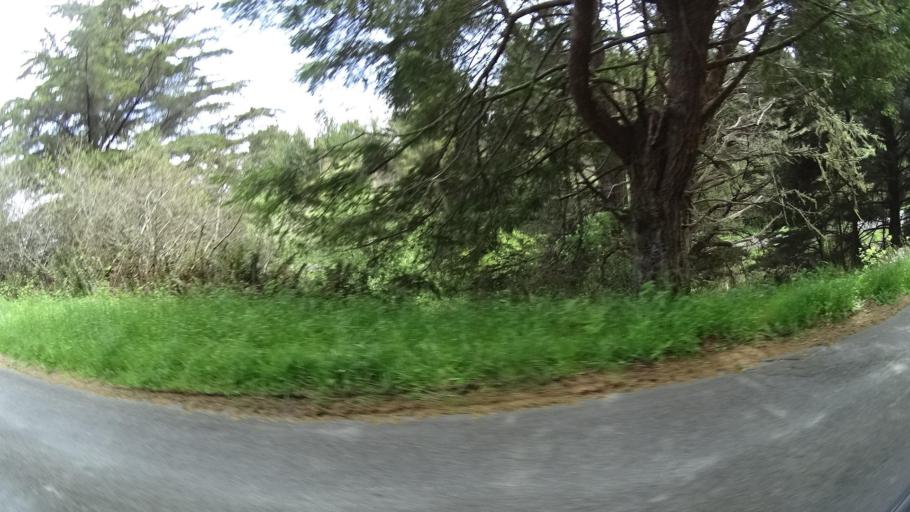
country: US
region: California
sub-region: Humboldt County
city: Humboldt Hill
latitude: 40.6861
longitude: -124.2358
